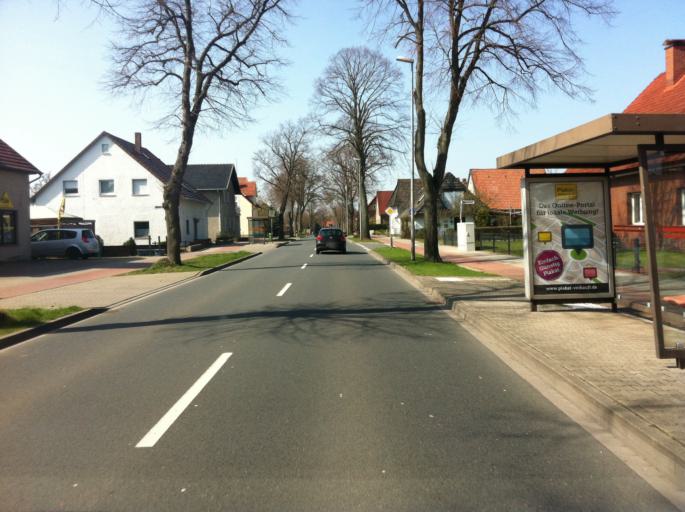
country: DE
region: North Rhine-Westphalia
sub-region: Regierungsbezirk Detmold
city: Minden
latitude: 52.2942
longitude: 8.8754
